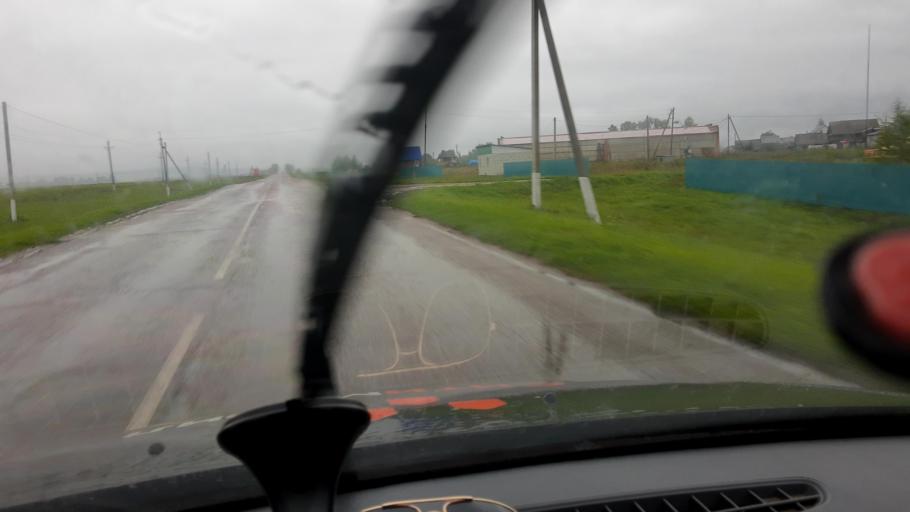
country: RU
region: Bashkortostan
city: Karmaskaly
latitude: 53.9796
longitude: 56.3906
